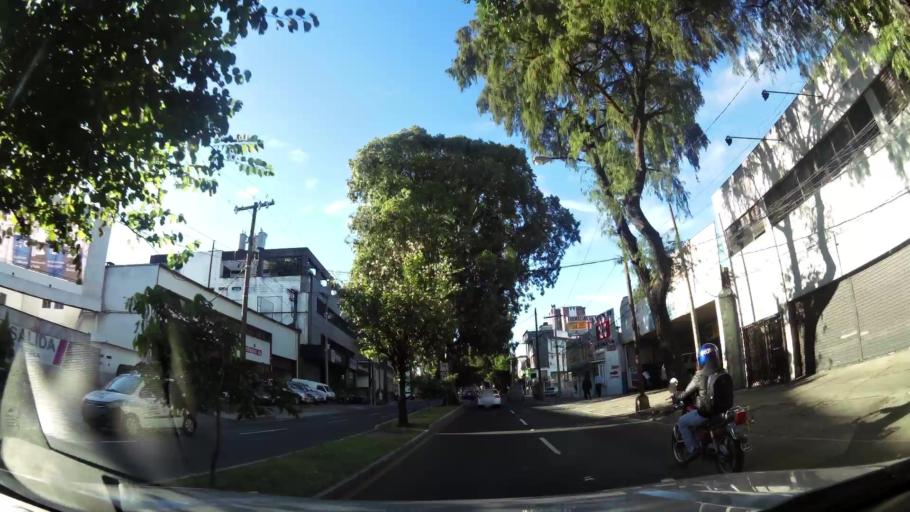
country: GT
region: Guatemala
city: Guatemala City
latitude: 14.6188
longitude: -90.5129
